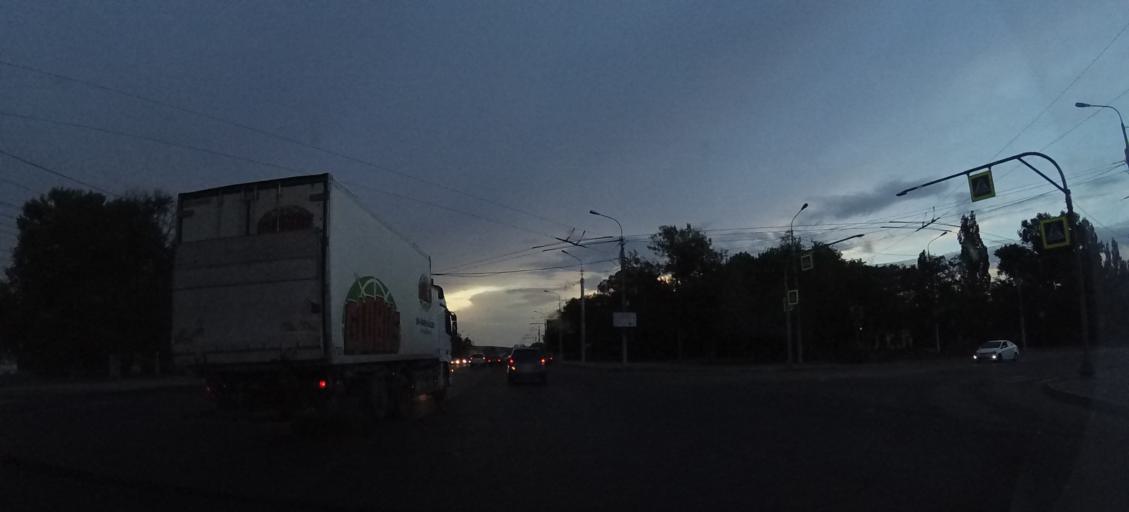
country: RU
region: Volgograd
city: Volgograd
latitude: 48.5821
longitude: 44.4226
